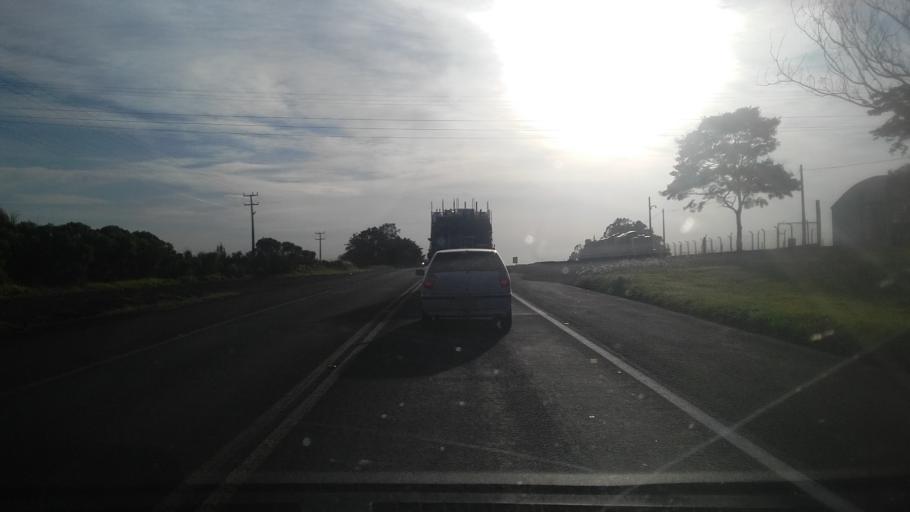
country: BR
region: Parana
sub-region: Bandeirantes
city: Bandeirantes
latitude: -23.1444
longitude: -50.5861
